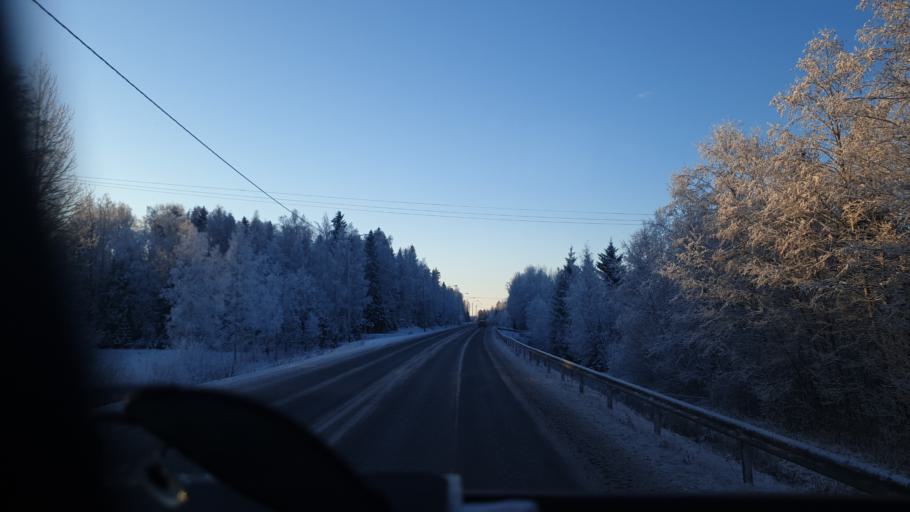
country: FI
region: Central Ostrobothnia
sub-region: Kokkola
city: Kaelviae
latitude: 63.9247
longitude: 23.4221
